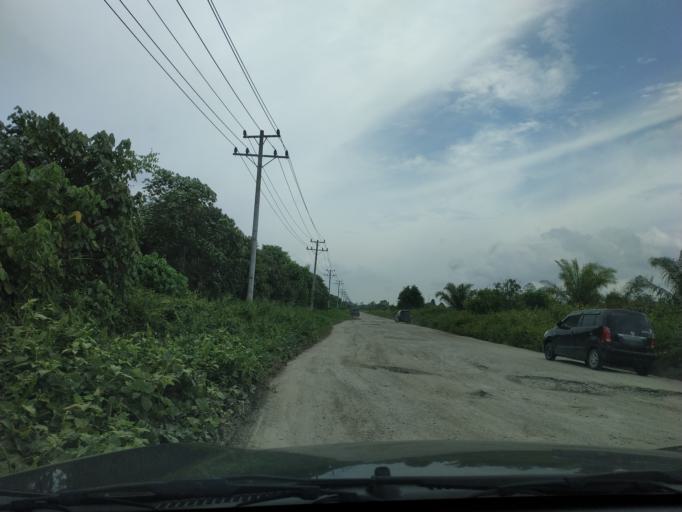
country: ID
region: Riau
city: Siak Sri Indrapura
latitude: 0.9128
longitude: 102.3029
